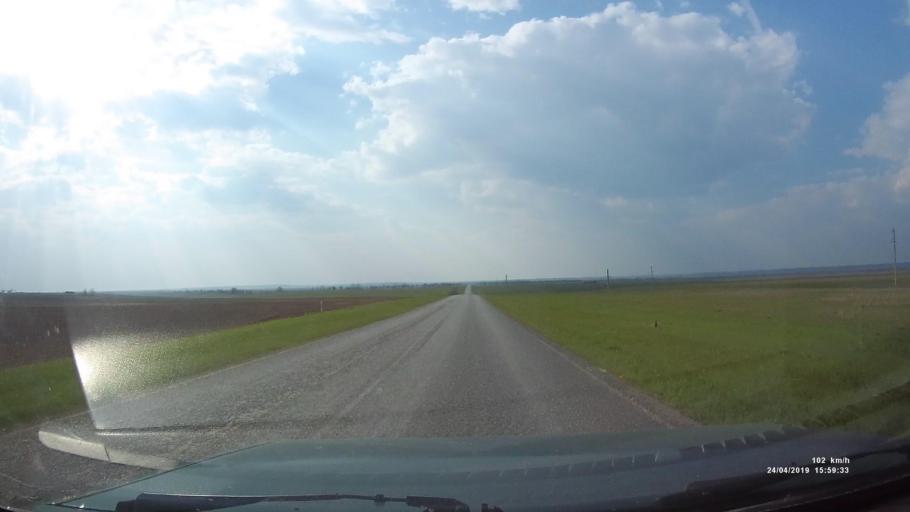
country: RU
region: Rostov
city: Sovetskoye
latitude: 46.6244
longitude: 42.4701
